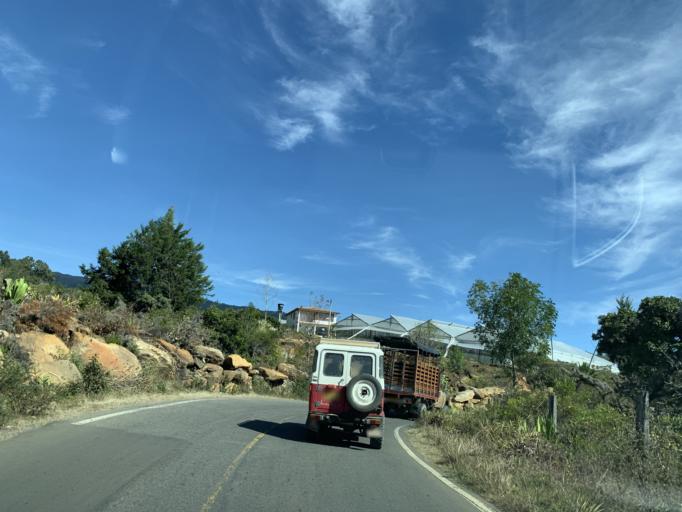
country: CO
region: Boyaca
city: Villa de Leiva
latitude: 5.6764
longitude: -73.5859
